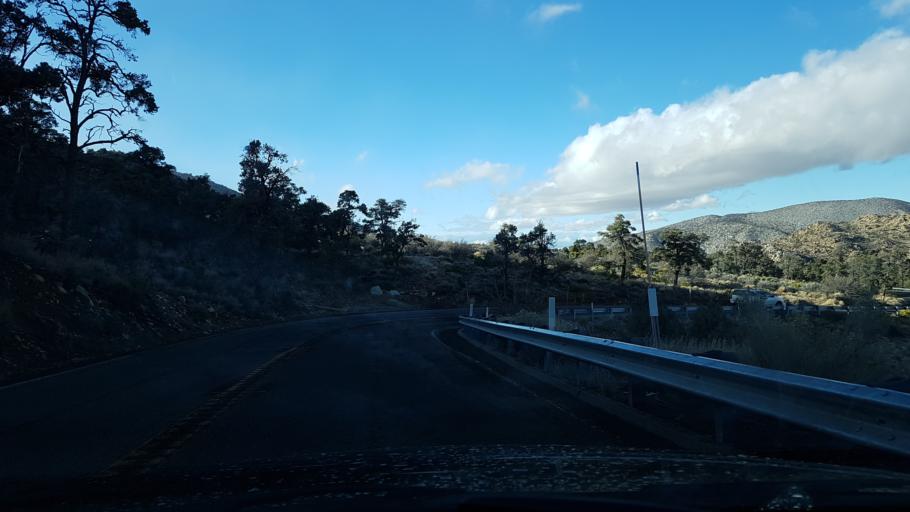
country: US
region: California
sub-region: San Bernardino County
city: Big Bear City
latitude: 34.3040
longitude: -116.8041
